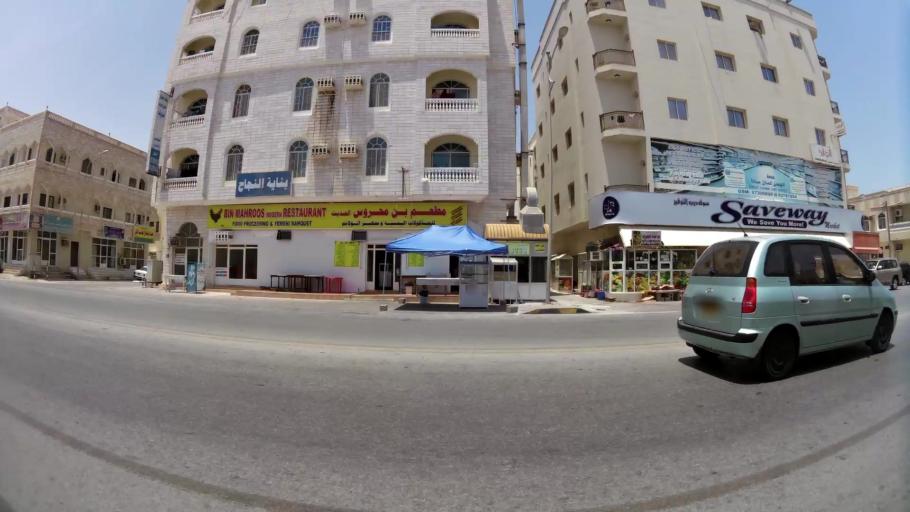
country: OM
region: Zufar
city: Salalah
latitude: 17.0209
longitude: 54.0844
